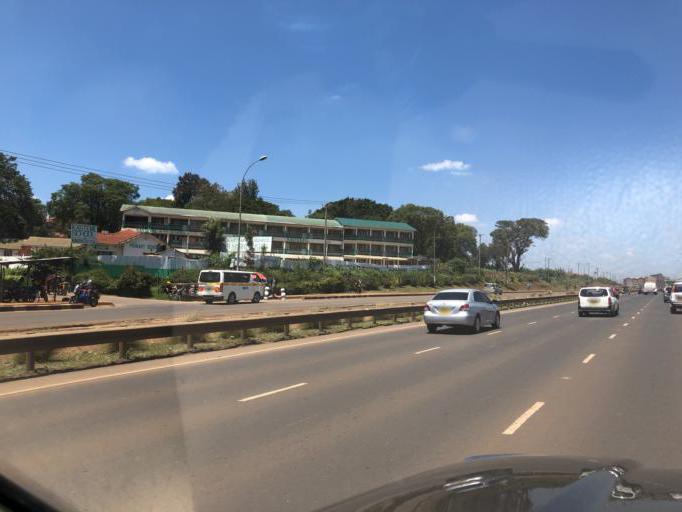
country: KE
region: Kiambu
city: Kiambu
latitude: -1.2122
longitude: 36.9040
